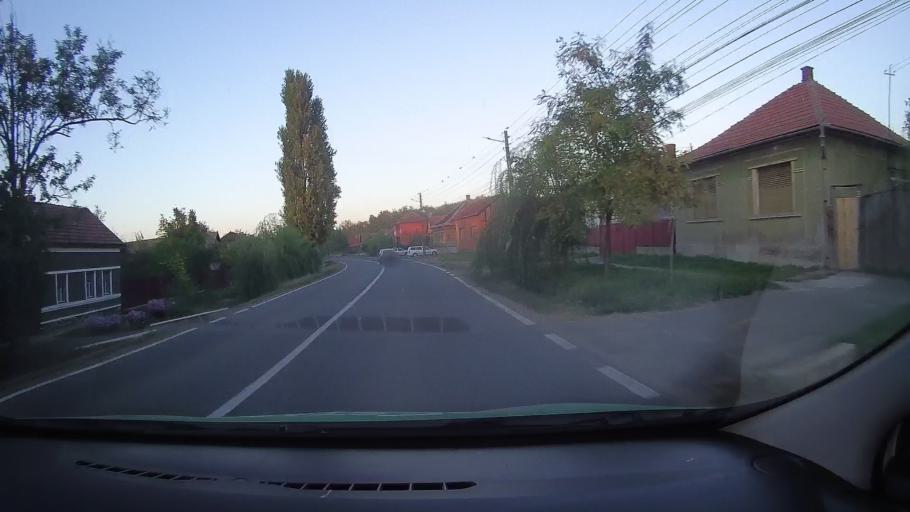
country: RO
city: Szekelyhid
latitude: 47.3566
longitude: 22.1109
